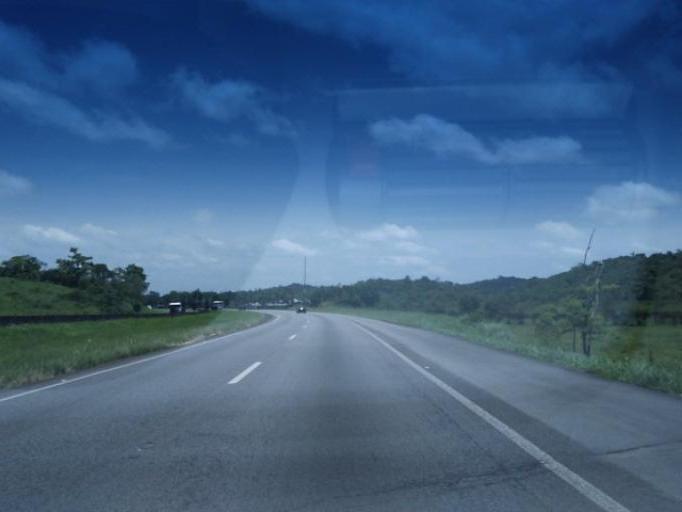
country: BR
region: Sao Paulo
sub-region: Registro
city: Registro
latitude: -24.4220
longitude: -47.7763
